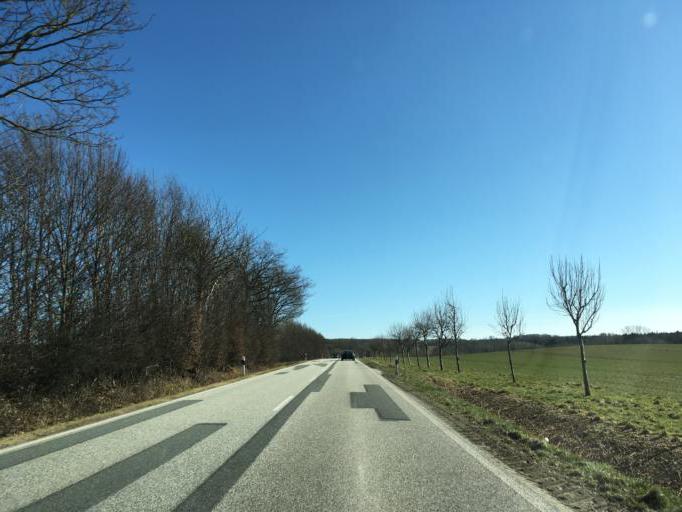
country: DE
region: Schleswig-Holstein
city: Berkenthin
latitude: 53.7285
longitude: 10.6569
